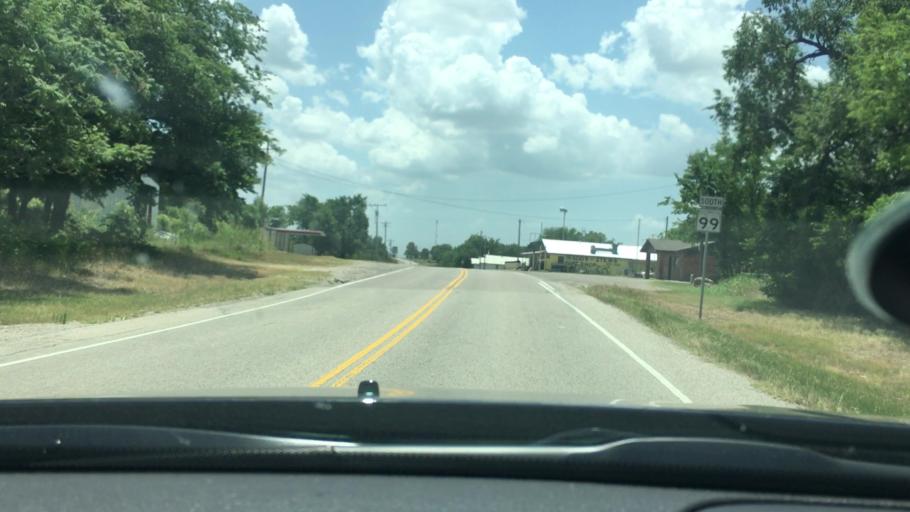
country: US
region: Oklahoma
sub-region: Johnston County
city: Tishomingo
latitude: 34.4504
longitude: -96.6362
